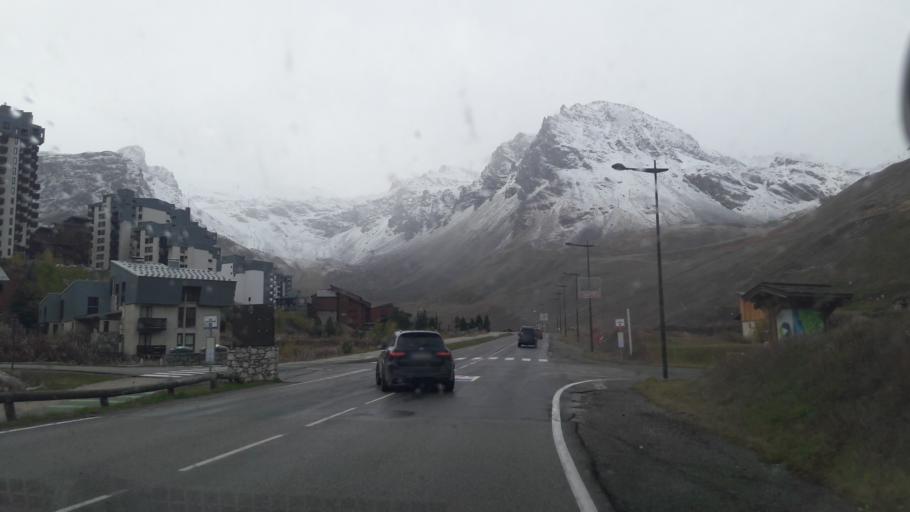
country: FR
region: Rhone-Alpes
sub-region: Departement de la Savoie
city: Tignes
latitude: 45.4606
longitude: 6.9004
